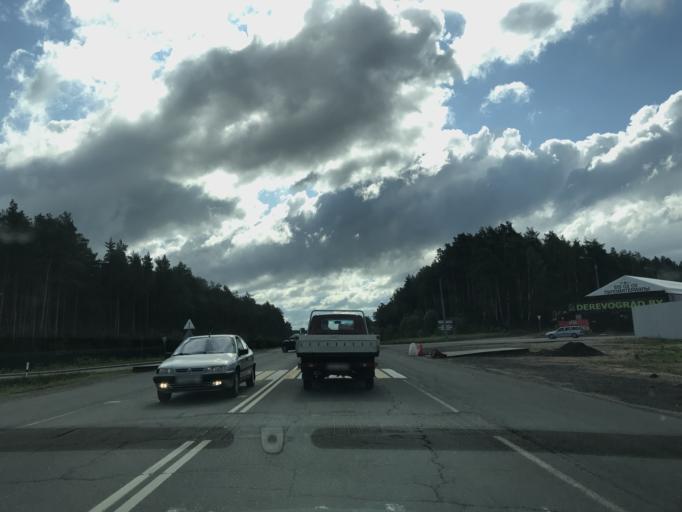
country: BY
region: Minsk
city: Borovlyany
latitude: 53.9678
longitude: 27.6308
